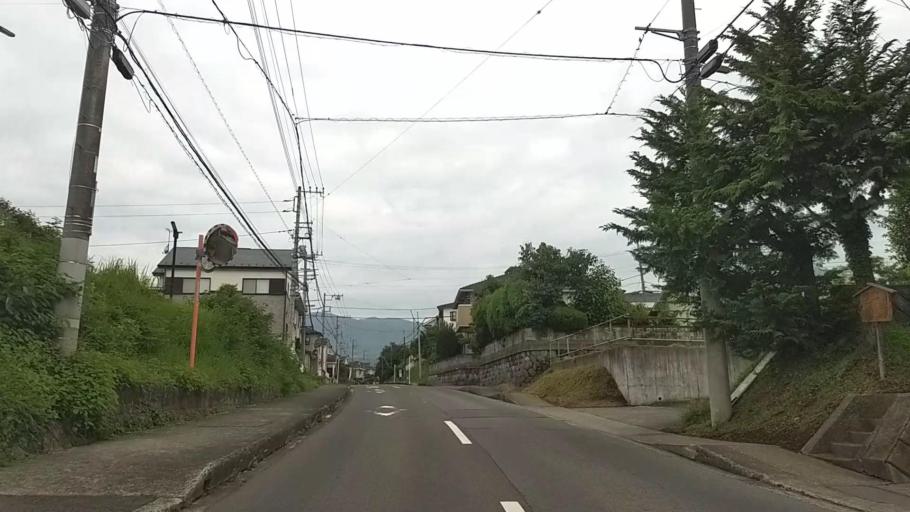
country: JP
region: Kanagawa
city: Odawara
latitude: 35.3239
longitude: 139.0982
